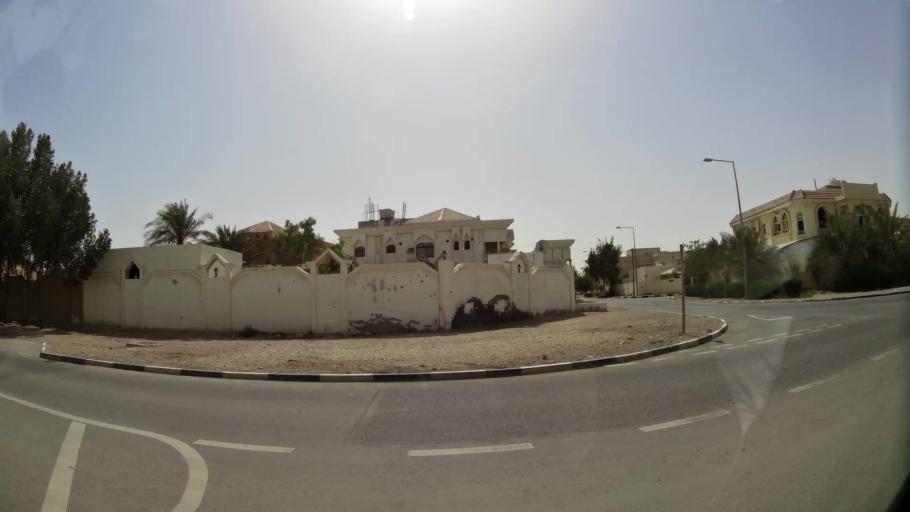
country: QA
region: Baladiyat Umm Salal
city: Umm Salal Muhammad
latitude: 25.3928
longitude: 51.4285
